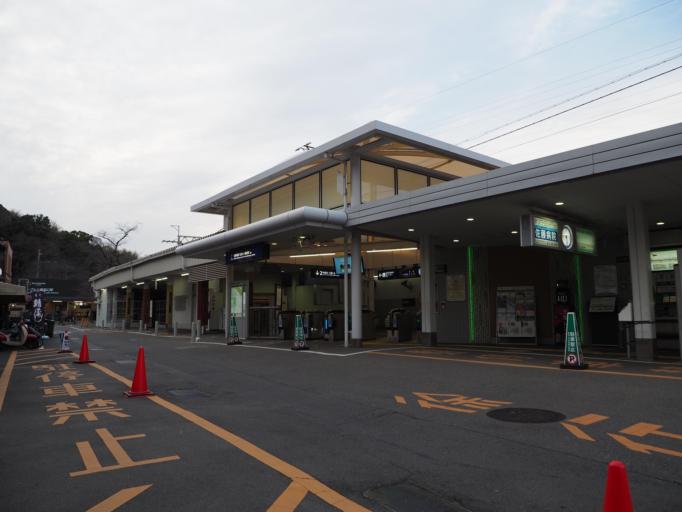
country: JP
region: Kyoto
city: Yawata
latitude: 34.8843
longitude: 135.7005
